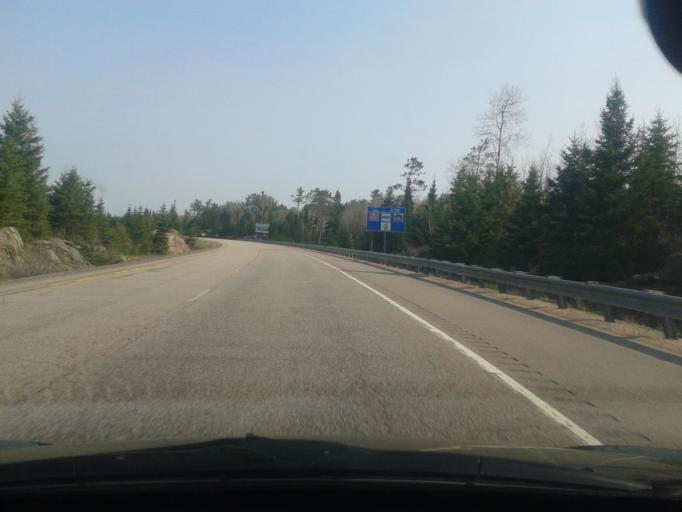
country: CA
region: Ontario
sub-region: Nipissing District
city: North Bay
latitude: 46.2317
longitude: -79.3489
